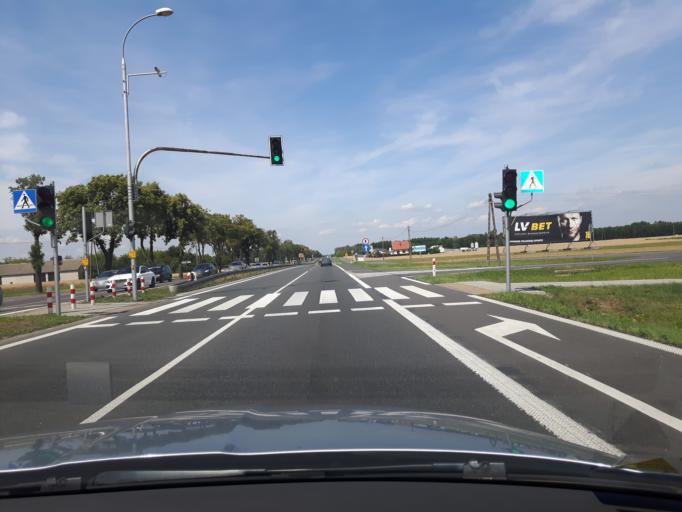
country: PL
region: Masovian Voivodeship
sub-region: Powiat plonski
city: Zaluski
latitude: 52.5306
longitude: 20.5199
